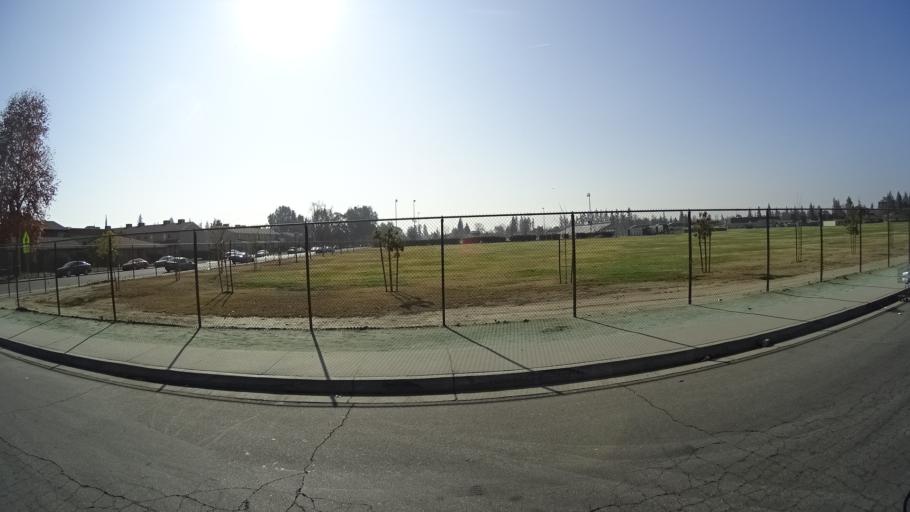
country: US
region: California
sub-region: Kern County
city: Bakersfield
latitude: 35.3454
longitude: -119.0554
